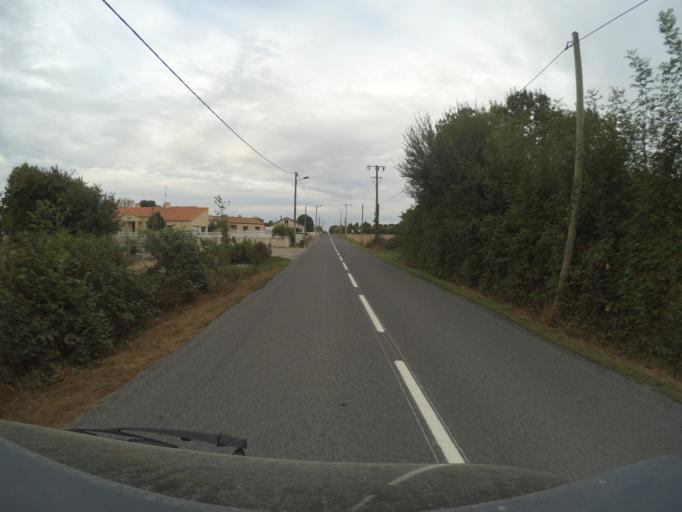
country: FR
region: Pays de la Loire
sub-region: Departement de la Loire-Atlantique
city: La Planche
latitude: 47.0151
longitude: -1.4386
